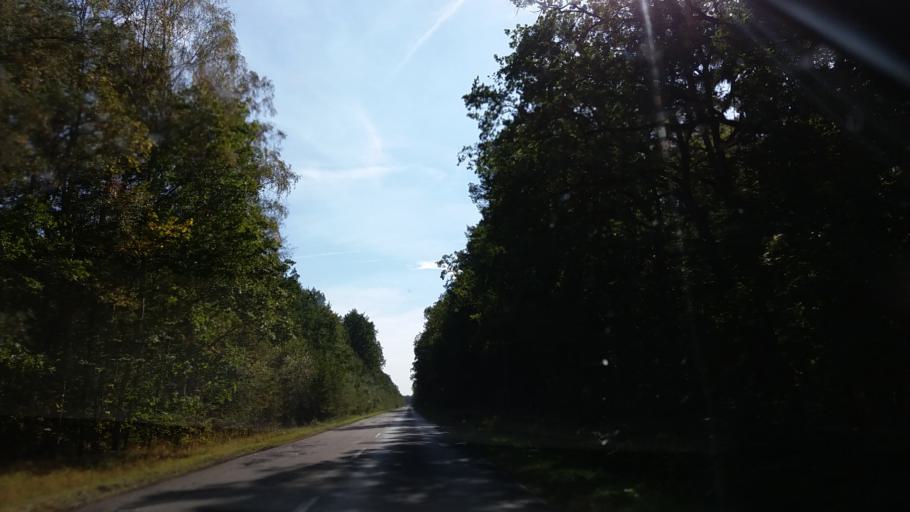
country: PL
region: Lubusz
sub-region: Powiat strzelecko-drezdenecki
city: Drezdenko
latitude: 52.8089
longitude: 15.8293
